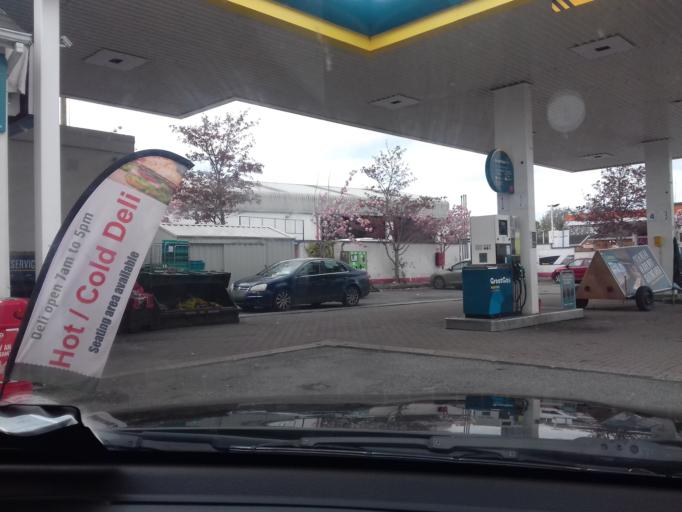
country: IE
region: Leinster
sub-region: Laois
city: Portlaoise
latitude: 53.0411
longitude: -7.3095
